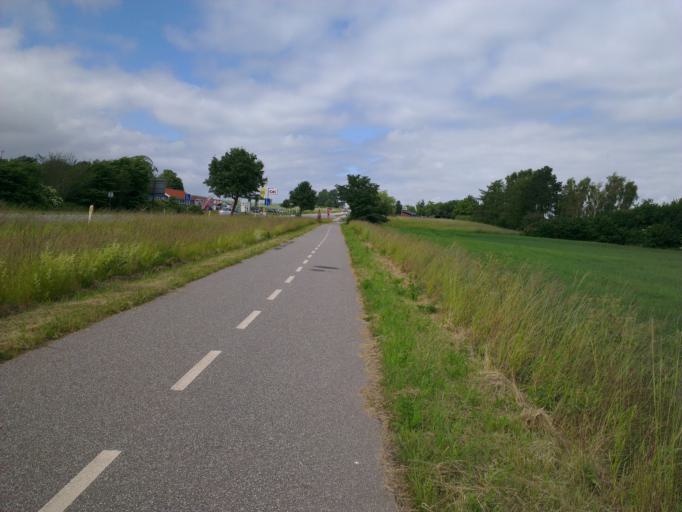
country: DK
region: Zealand
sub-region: Lejre Kommune
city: Lejre
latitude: 55.6518
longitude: 11.9221
